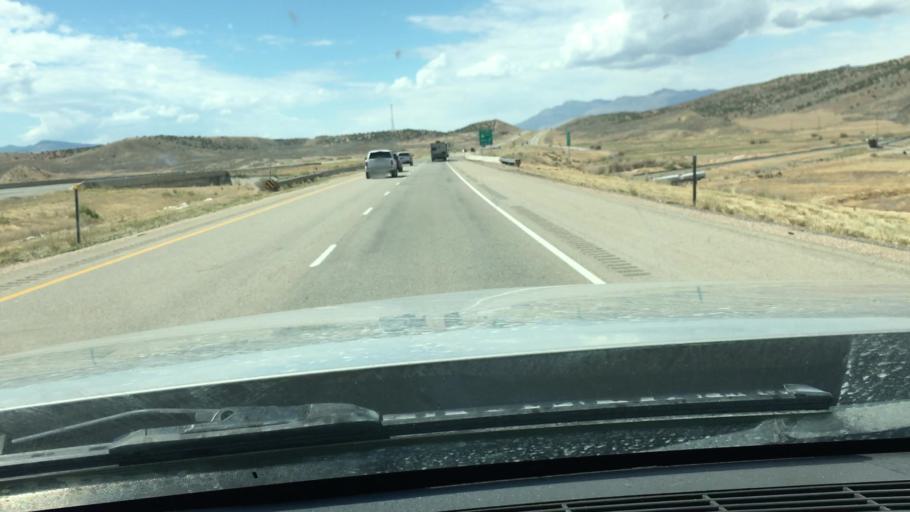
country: US
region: Utah
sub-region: Juab County
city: Nephi
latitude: 39.4888
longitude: -111.9734
